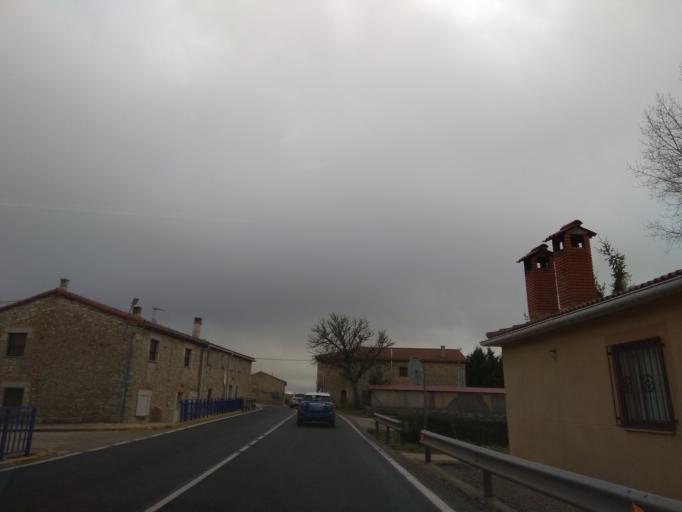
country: ES
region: Castille and Leon
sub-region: Provincia de Burgos
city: Tubilla del Agua
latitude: 42.6466
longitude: -3.8845
